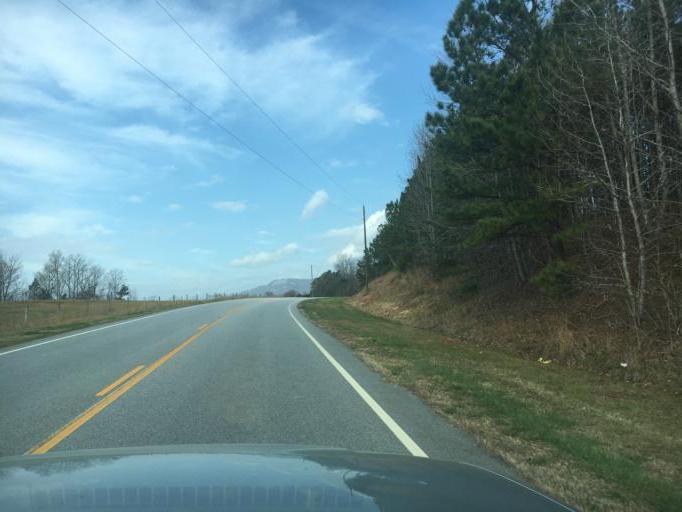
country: US
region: North Carolina
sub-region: Polk County
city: Tryon
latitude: 35.1250
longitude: -82.2629
